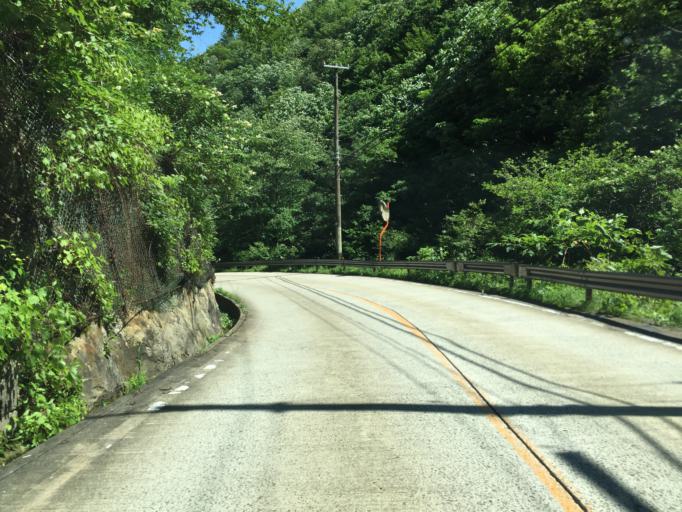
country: JP
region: Fukushima
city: Fukushima-shi
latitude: 37.7510
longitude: 140.3151
